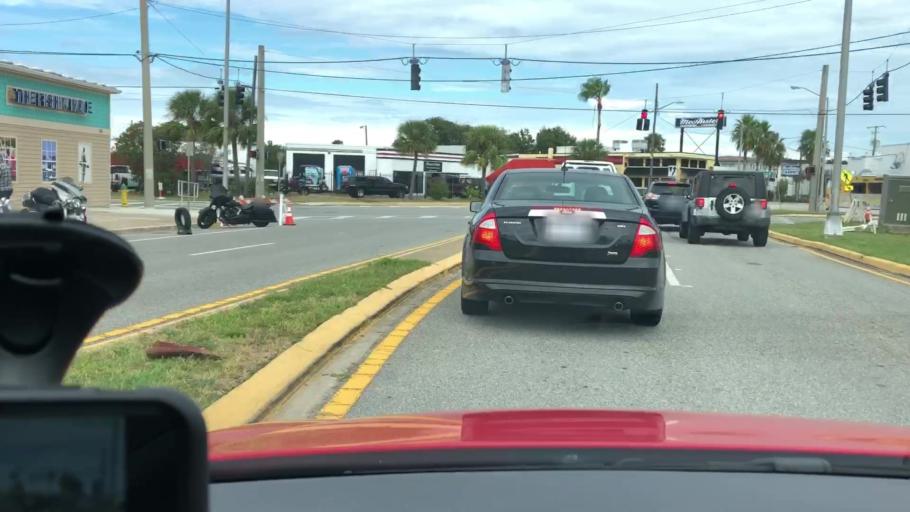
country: US
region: Florida
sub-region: Volusia County
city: Daytona Beach
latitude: 29.2210
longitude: -81.0226
